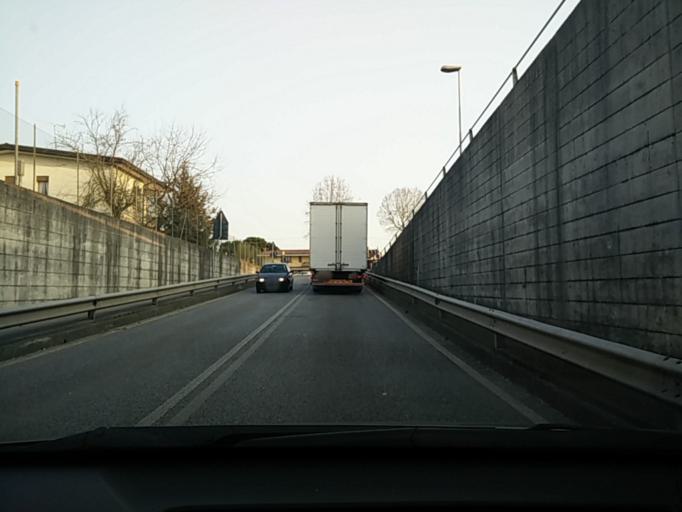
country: IT
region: Veneto
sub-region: Provincia di Treviso
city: Ponte di Piave
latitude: 45.7060
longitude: 12.4395
